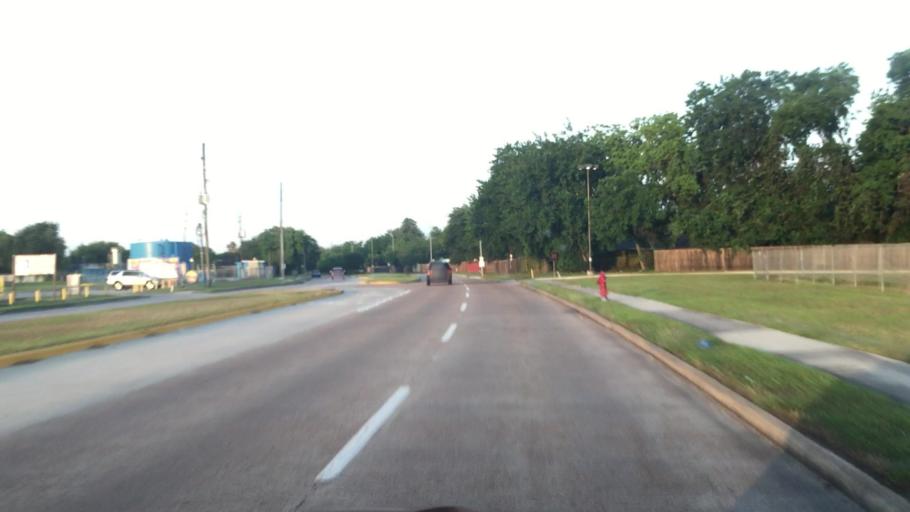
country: US
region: Texas
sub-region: Harris County
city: Hudson
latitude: 29.9594
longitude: -95.4809
